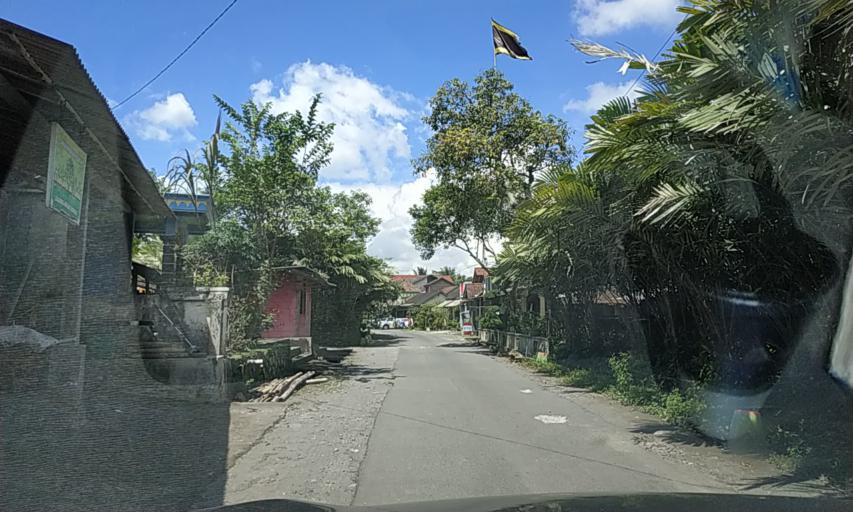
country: ID
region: Central Java
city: Muntilan
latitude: -7.5953
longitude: 110.3512
